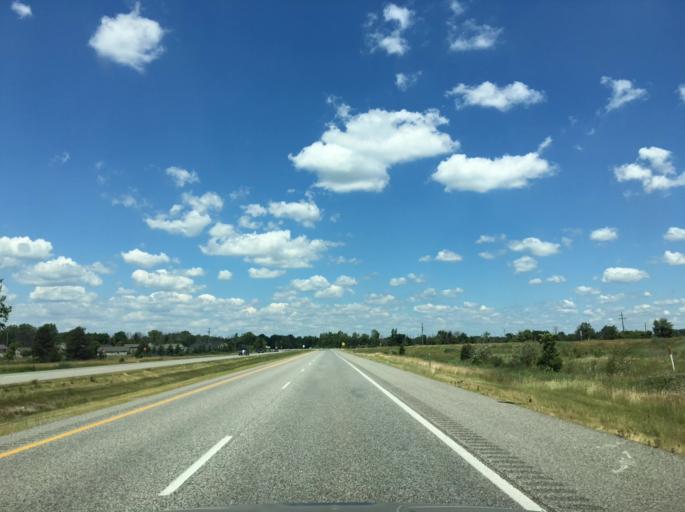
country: US
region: Michigan
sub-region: Midland County
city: Midland
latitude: 43.6408
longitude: -84.1874
